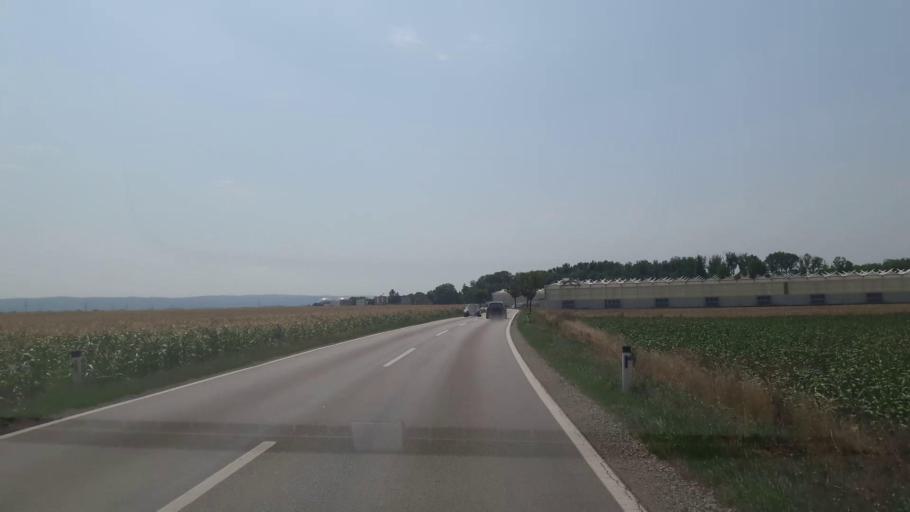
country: AT
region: Lower Austria
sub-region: Politischer Bezirk Bruck an der Leitha
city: Enzersdorf an der Fischa
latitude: 48.0600
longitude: 16.6094
